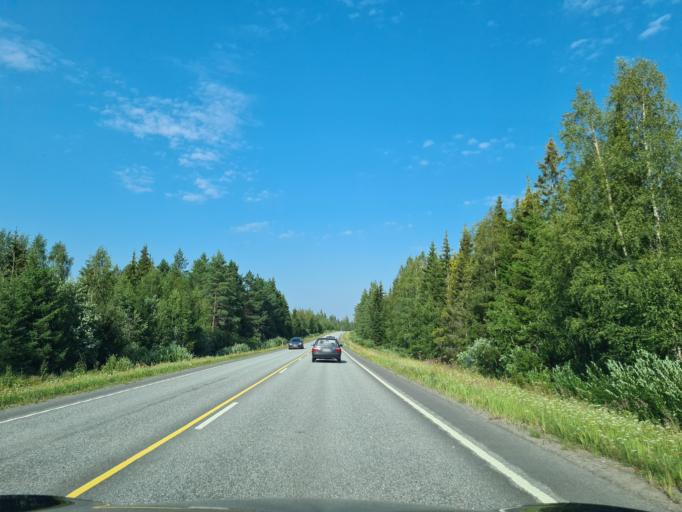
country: FI
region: Satakunta
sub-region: Pori
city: Laengelmaeki
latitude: 61.7614
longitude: 22.1418
